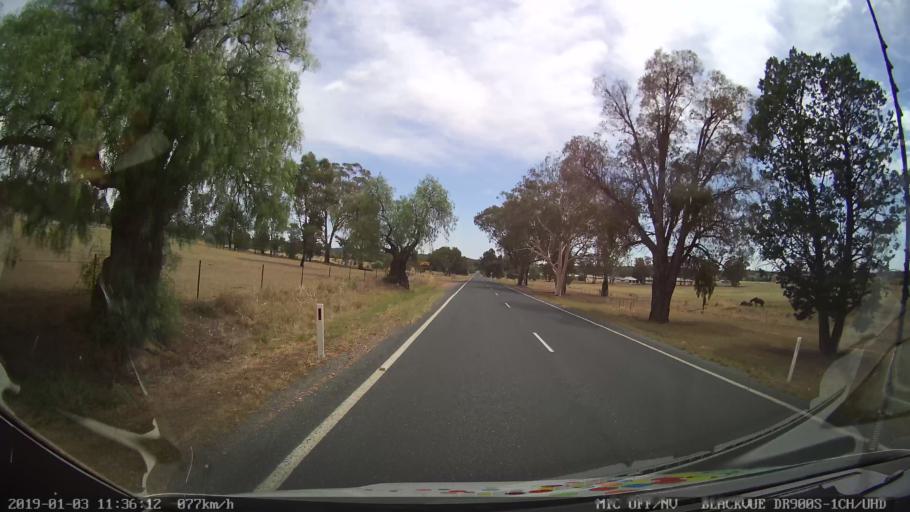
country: AU
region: New South Wales
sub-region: Weddin
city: Grenfell
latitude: -33.9134
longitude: 148.1595
